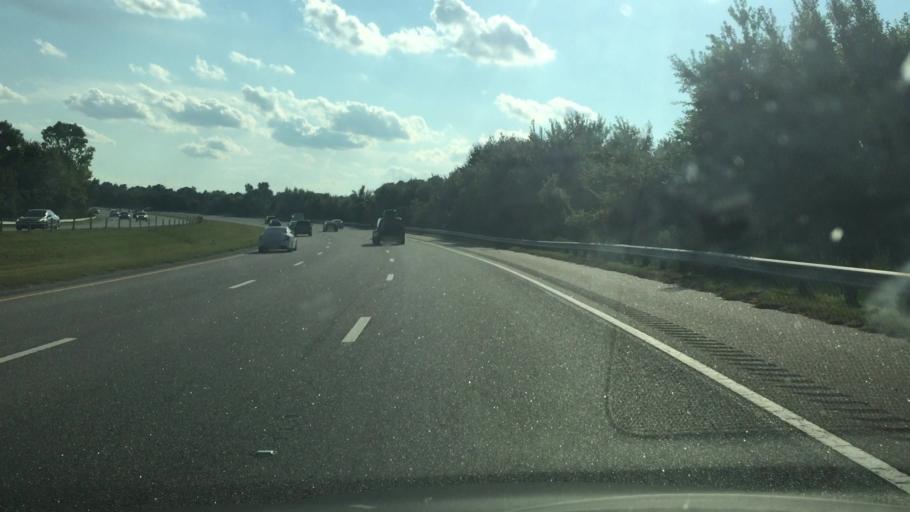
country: US
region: South Carolina
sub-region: Horry County
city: North Myrtle Beach
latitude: 33.8256
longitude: -78.7314
